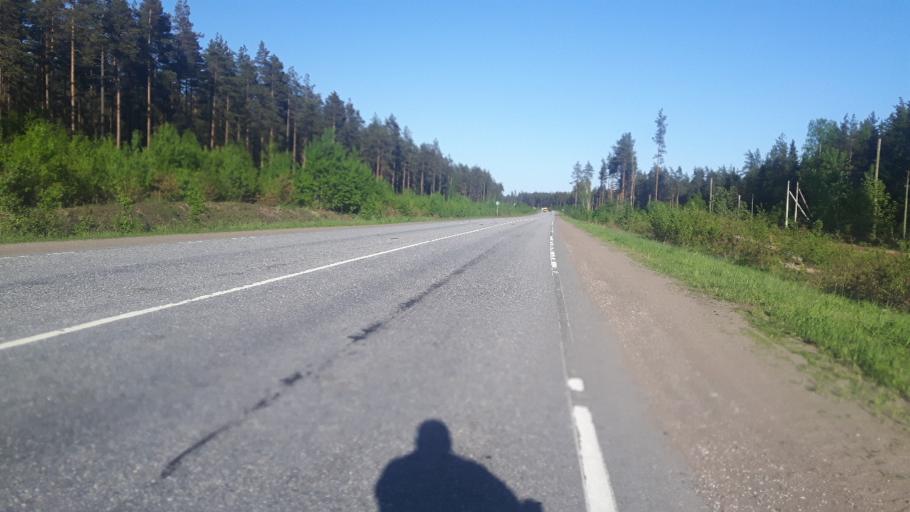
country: RU
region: Leningrad
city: Molodezhnoye
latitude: 60.1728
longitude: 29.2935
